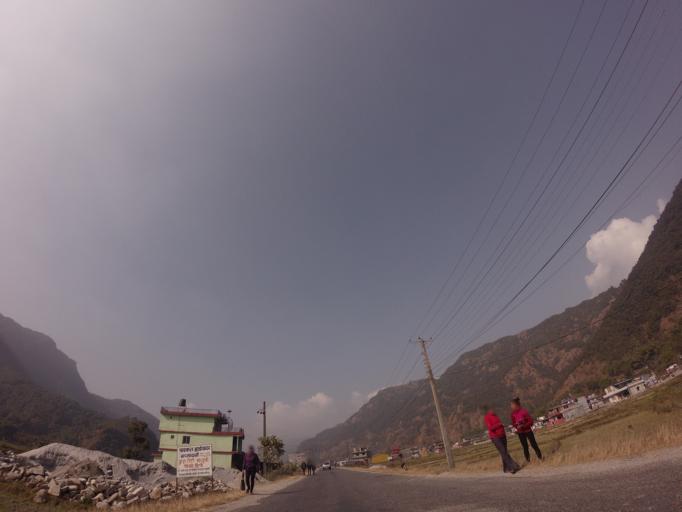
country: NP
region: Western Region
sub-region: Gandaki Zone
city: Pokhara
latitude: 28.2822
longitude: 83.9252
